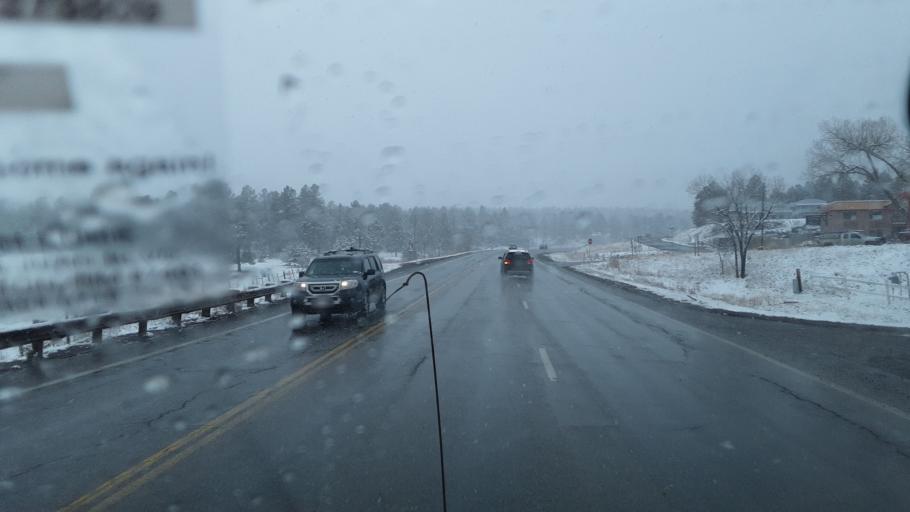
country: US
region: Colorado
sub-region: Archuleta County
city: Pagosa Springs
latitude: 37.2670
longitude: -107.0234
